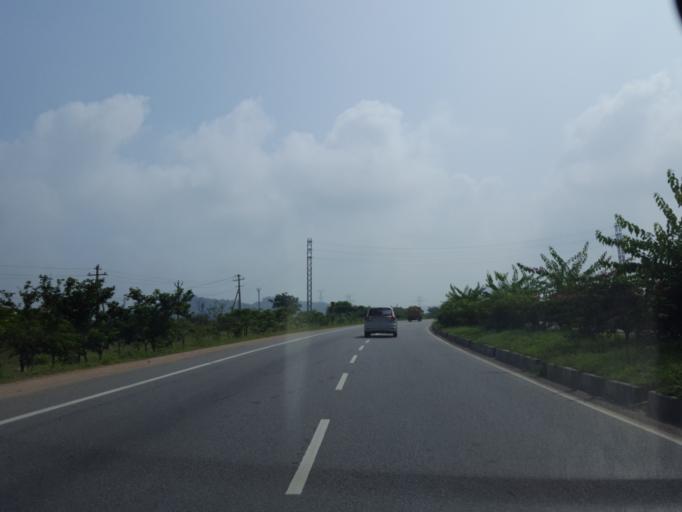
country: IN
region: Telangana
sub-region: Rangareddi
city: Ghatkesar
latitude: 17.2810
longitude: 78.8001
